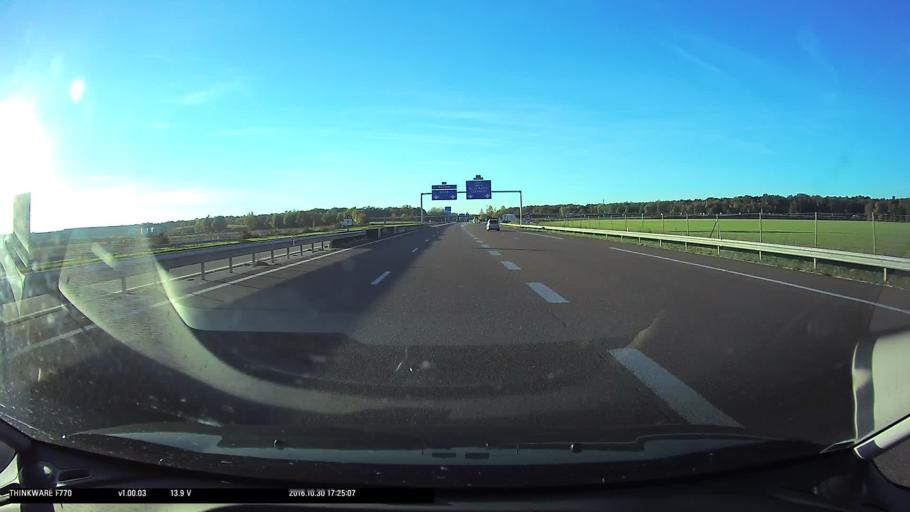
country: FR
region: Bourgogne
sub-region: Departement de la Cote-d'Or
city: Chevigny-Saint-Sauveur
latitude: 47.2726
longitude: 5.1519
